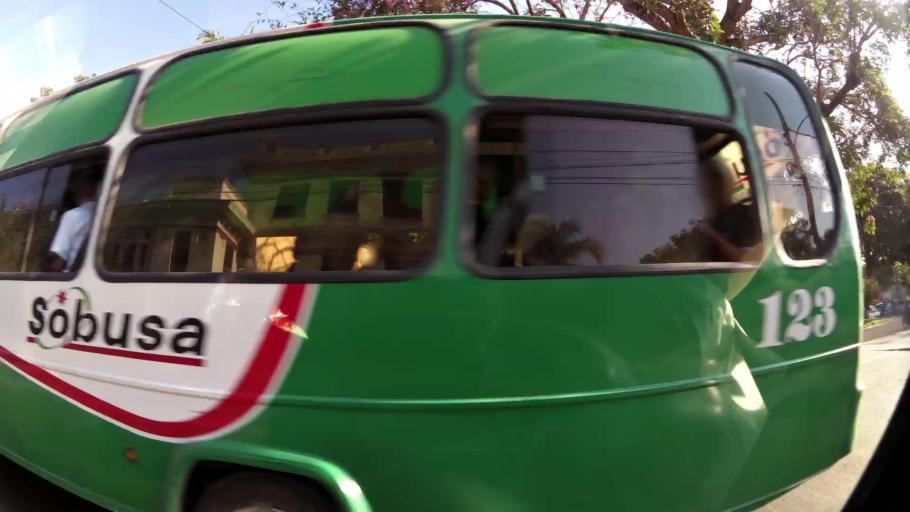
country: CO
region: Atlantico
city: Barranquilla
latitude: 10.9962
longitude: -74.8021
